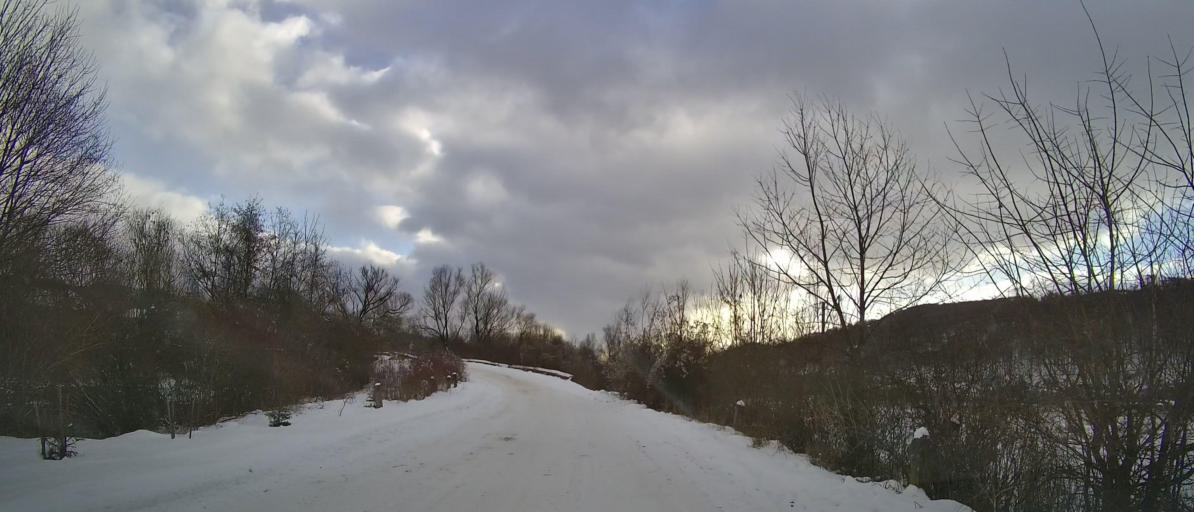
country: UA
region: Zakarpattia
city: Velykyi Bereznyi
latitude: 48.9224
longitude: 22.4627
